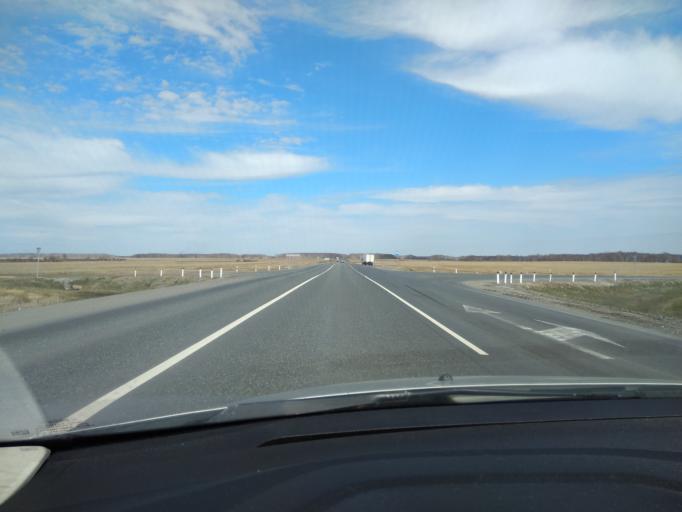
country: RU
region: Sverdlovsk
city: Pyshma
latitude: 56.9156
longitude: 63.1266
